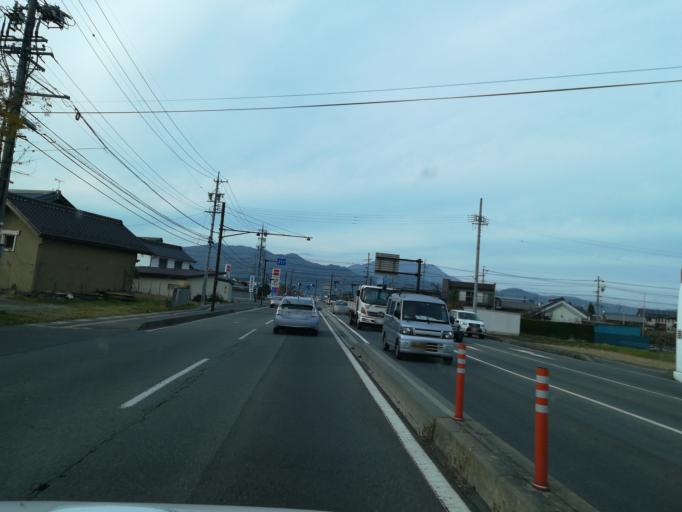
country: JP
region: Nagano
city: Nagano-shi
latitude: 36.5939
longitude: 138.1840
